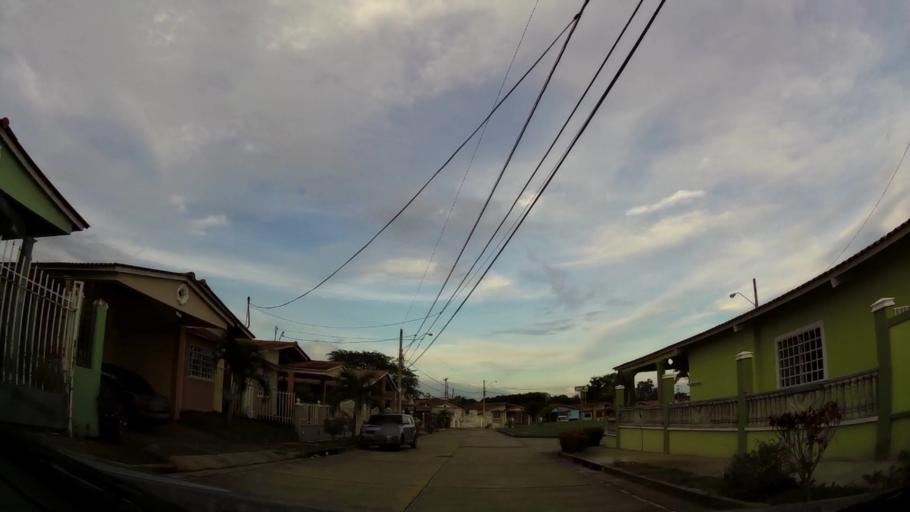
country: PA
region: Panama
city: La Chorrera
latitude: 8.8693
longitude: -79.7647
